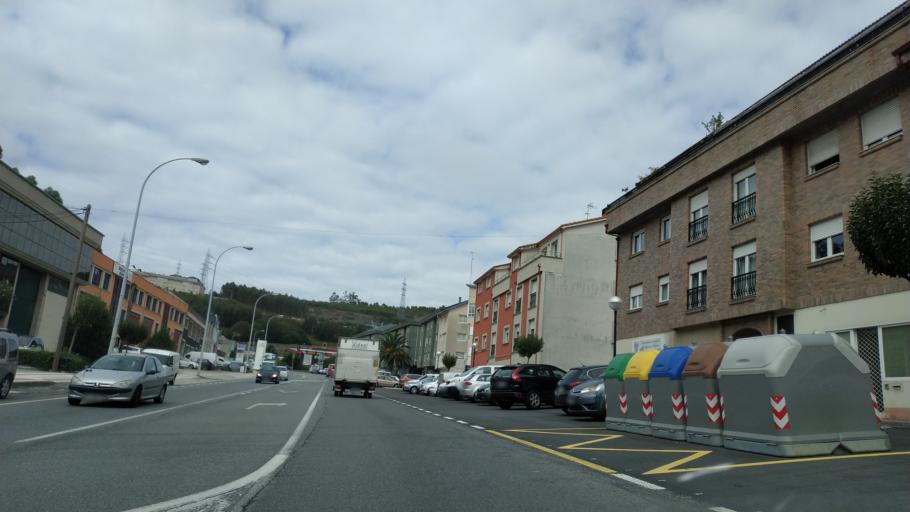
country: ES
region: Galicia
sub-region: Provincia da Coruna
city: Arteixo
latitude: 43.3215
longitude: -8.4738
